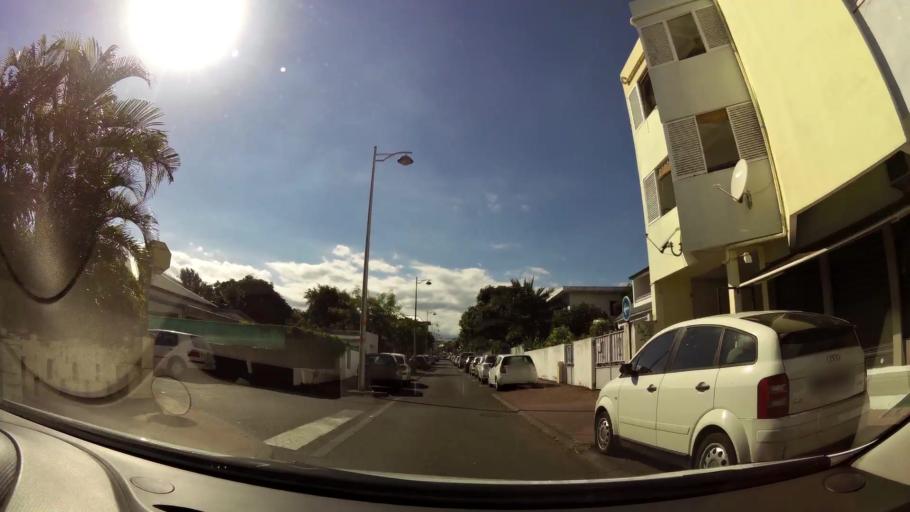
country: RE
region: Reunion
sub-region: Reunion
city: Saint-Pierre
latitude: -21.3402
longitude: 55.4705
